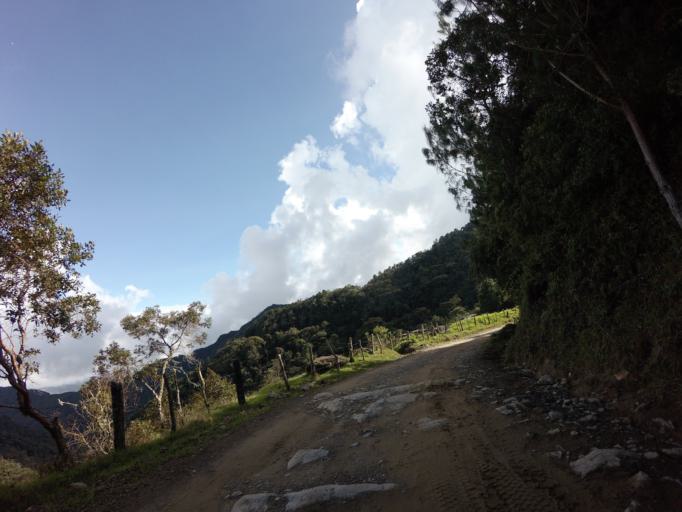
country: CO
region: Caldas
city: Pensilvania
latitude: 5.4564
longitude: -75.1240
